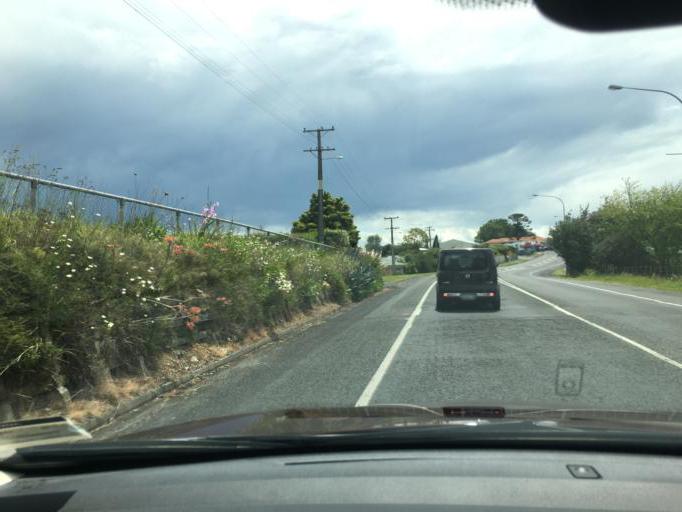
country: NZ
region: Waikato
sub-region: Waipa District
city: Cambridge
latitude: -37.9209
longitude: 175.3082
